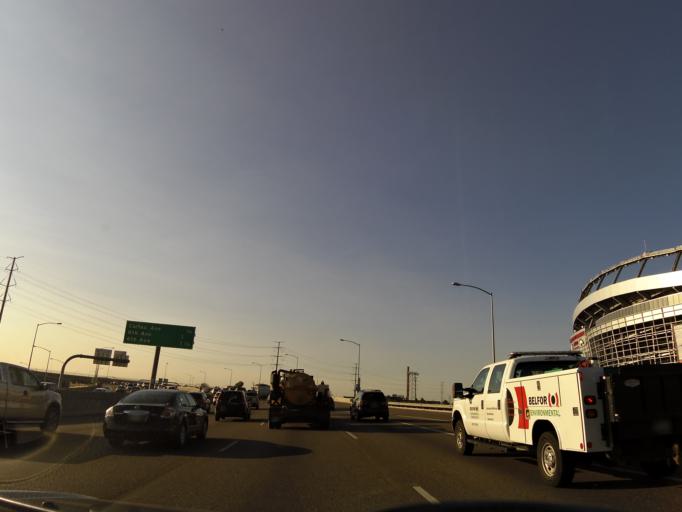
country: US
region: Colorado
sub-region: Denver County
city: Denver
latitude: 39.7459
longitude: -105.0182
